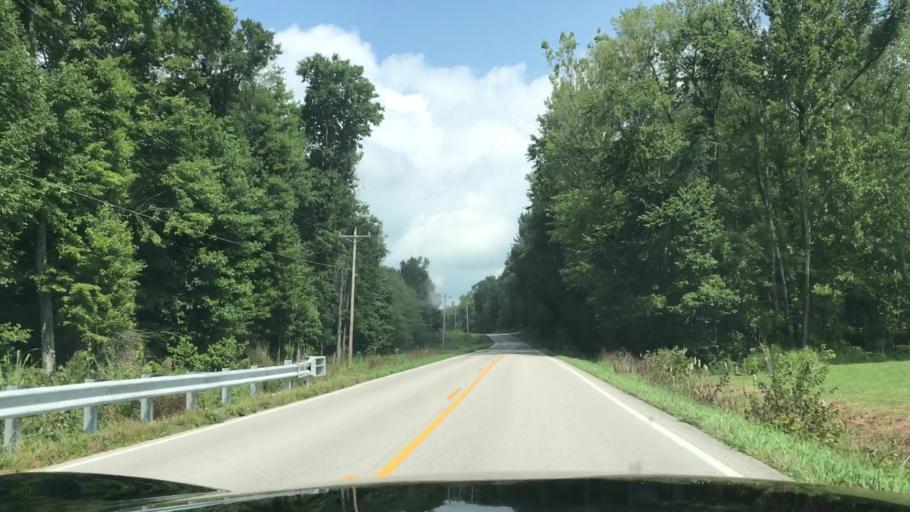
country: US
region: Kentucky
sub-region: Ohio County
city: Oak Grove
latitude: 37.1944
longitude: -86.8838
